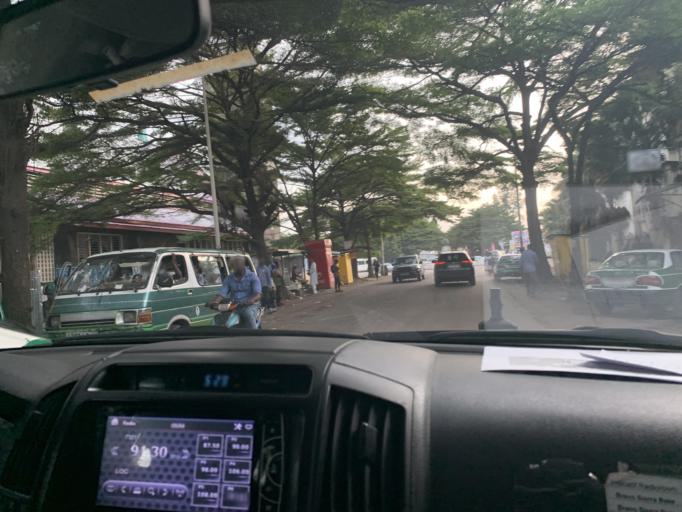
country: CG
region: Brazzaville
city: Brazzaville
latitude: -4.2665
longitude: 15.2852
